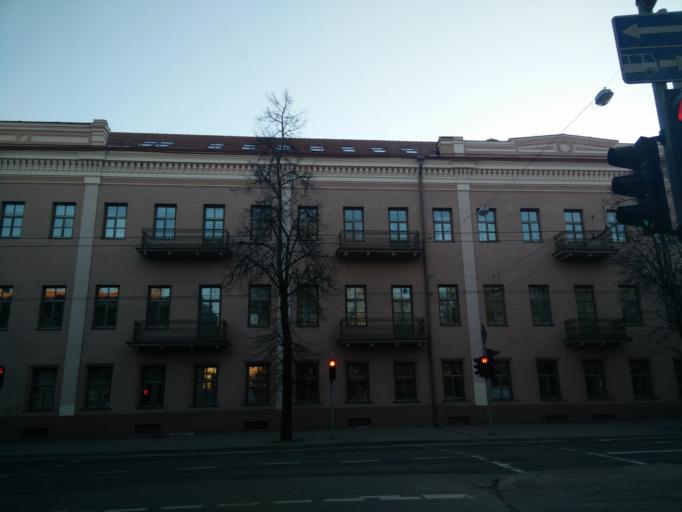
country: LT
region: Vilnius County
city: Naujamiestis
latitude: 54.6786
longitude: 25.2785
